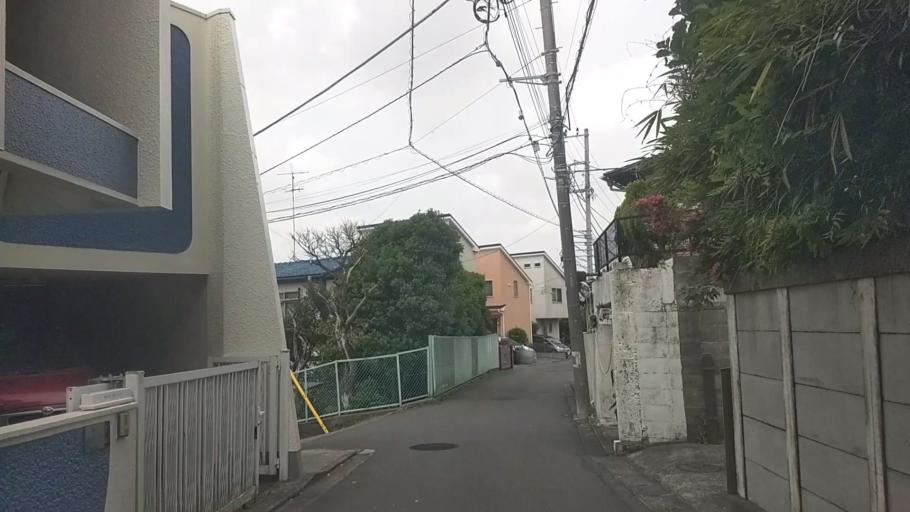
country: JP
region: Kanagawa
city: Fujisawa
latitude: 35.3829
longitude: 139.5111
